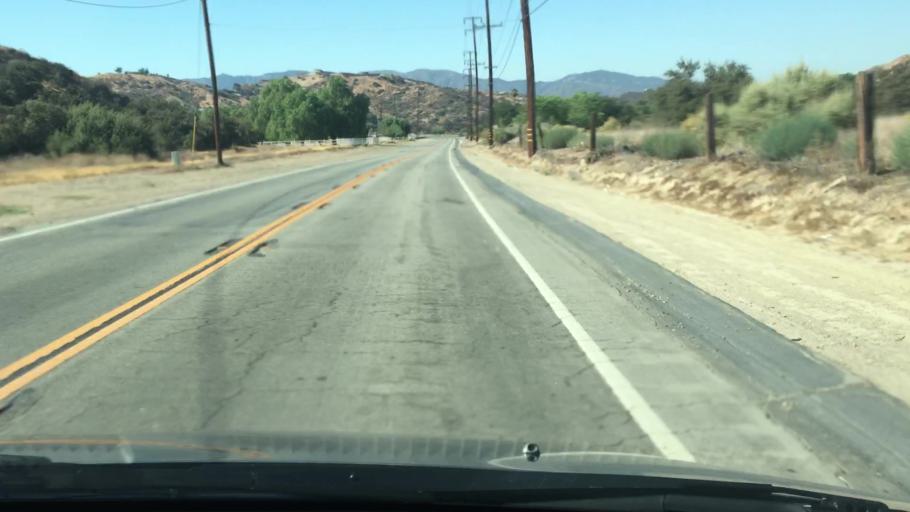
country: US
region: California
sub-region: Los Angeles County
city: Agua Dulce
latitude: 34.4594
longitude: -118.4211
